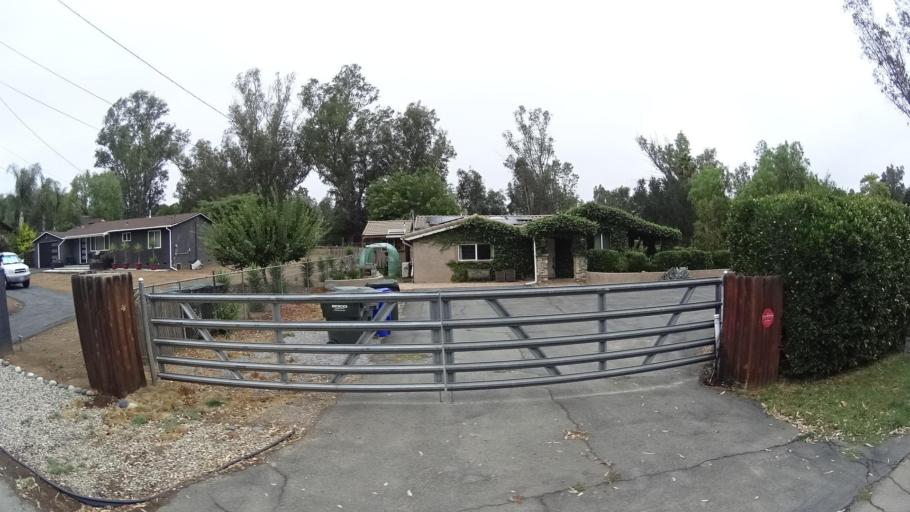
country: US
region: California
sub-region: San Diego County
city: Escondido
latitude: 33.1129
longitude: -117.1299
